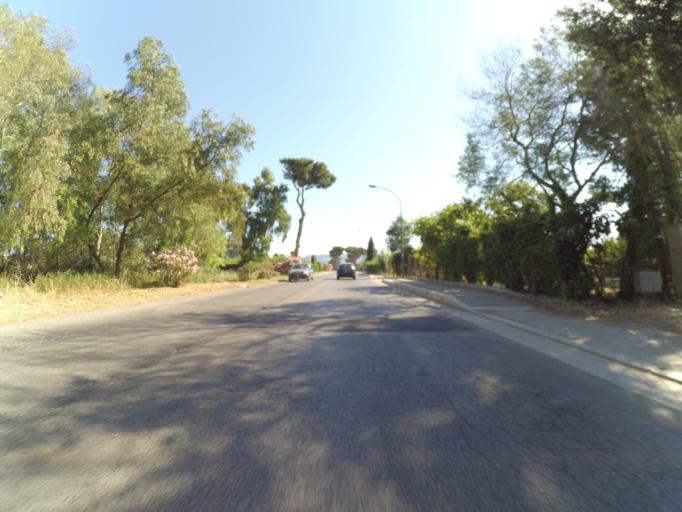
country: IT
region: Latium
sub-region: Provincia di Latina
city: San Felice Circeo
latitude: 41.2816
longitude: 13.1036
